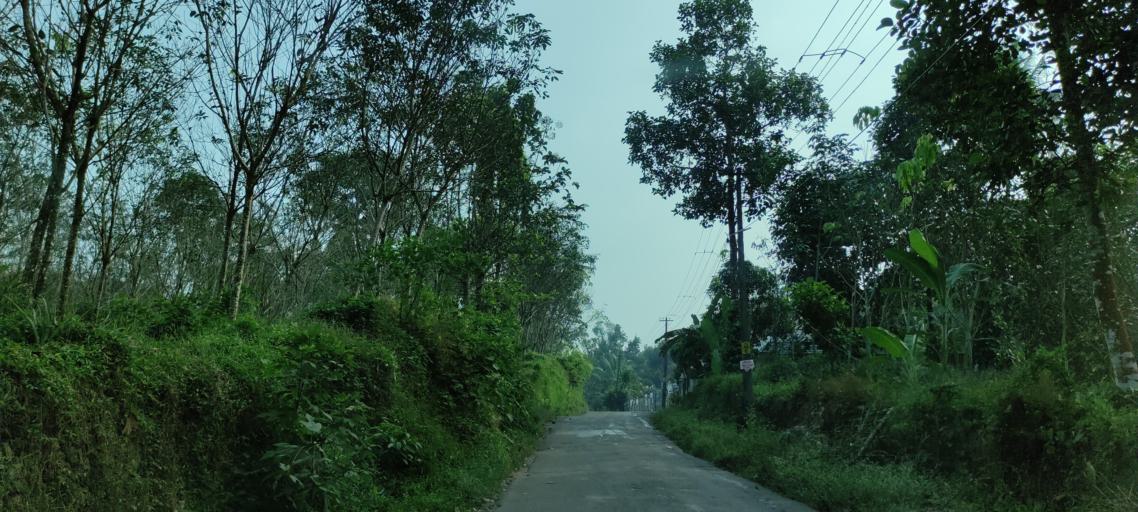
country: IN
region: Kerala
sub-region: Ernakulam
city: Piravam
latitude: 9.8100
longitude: 76.5343
